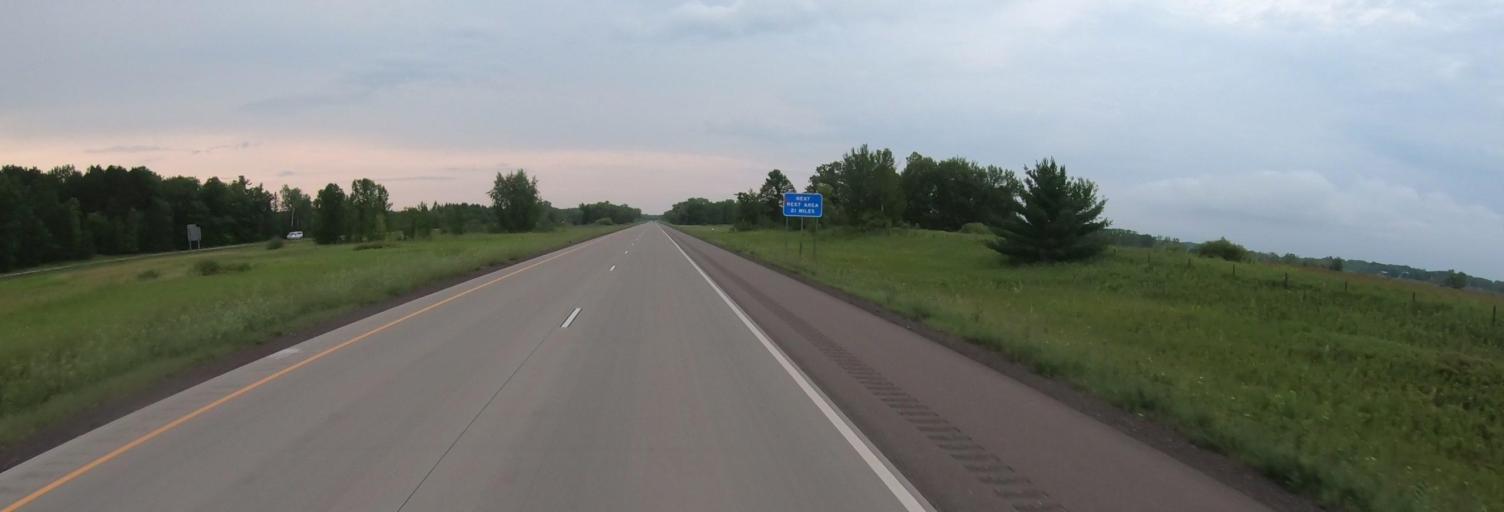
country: US
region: Minnesota
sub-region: Pine County
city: Hinckley
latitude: 45.9207
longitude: -92.9666
